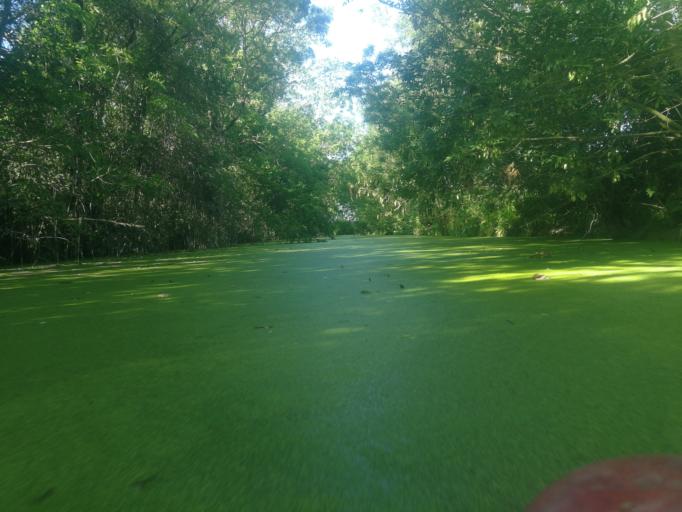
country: FR
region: Poitou-Charentes
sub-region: Departement de la Charente-Maritime
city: Marans
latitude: 46.3596
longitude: -0.9516
